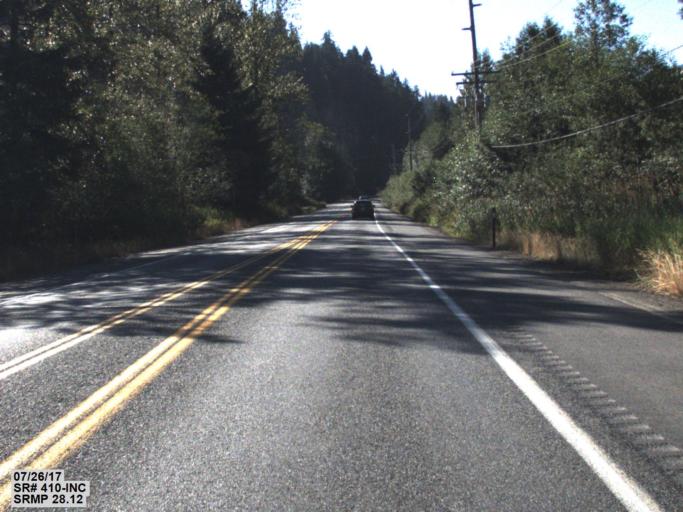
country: US
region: Washington
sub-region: King County
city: Enumclaw
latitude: 47.1814
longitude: -121.9224
